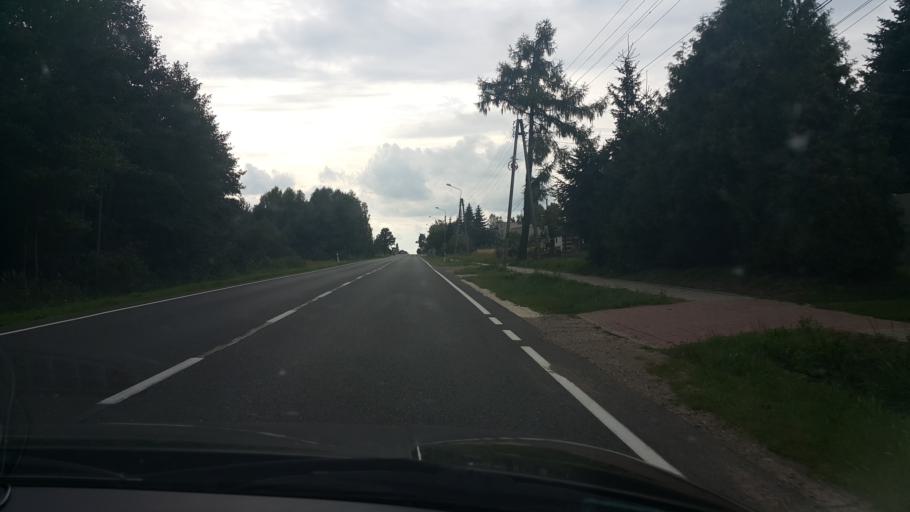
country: PL
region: Swietokrzyskie
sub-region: Powiat skarzyski
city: Blizyn
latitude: 51.1017
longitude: 20.7856
